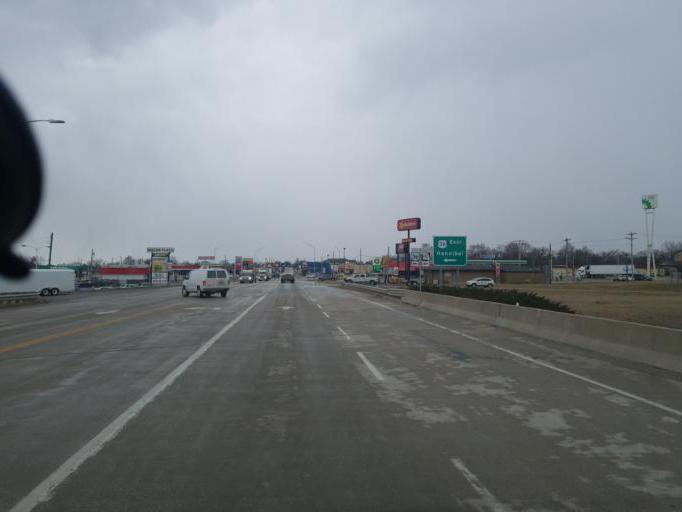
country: US
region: Missouri
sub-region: Macon County
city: Macon
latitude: 39.7542
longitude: -92.4678
